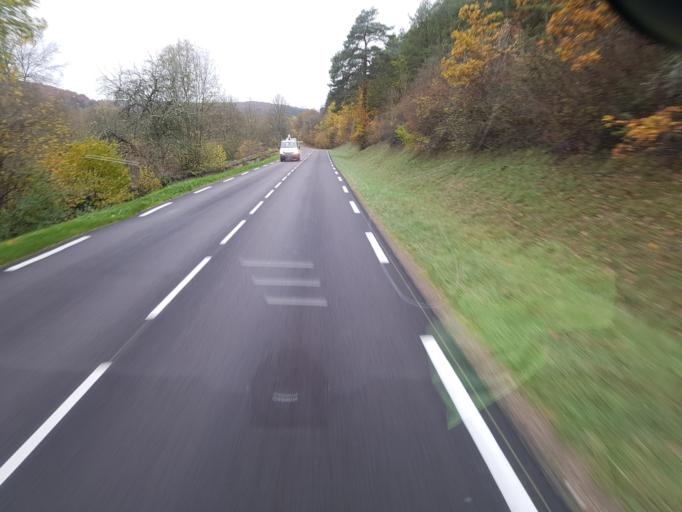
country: FR
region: Bourgogne
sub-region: Departement de la Cote-d'Or
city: Messigny-et-Vantoux
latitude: 47.5402
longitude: 4.9454
